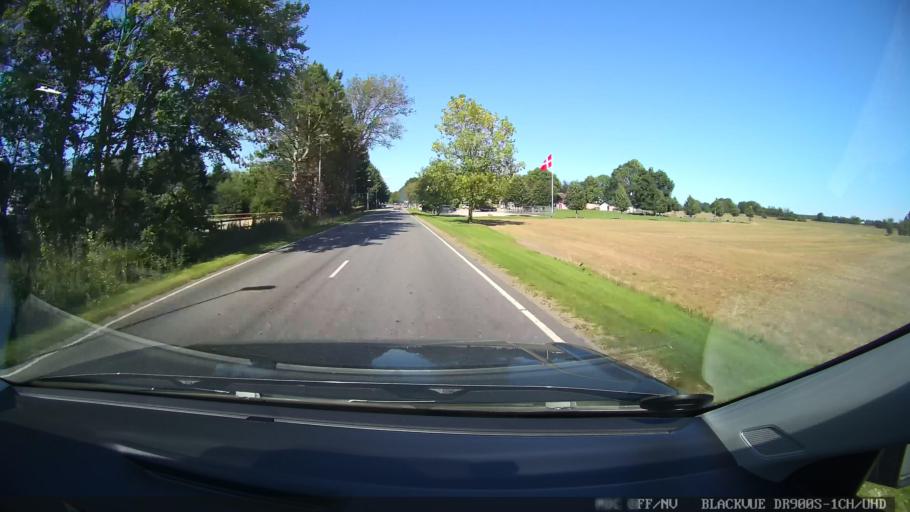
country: DK
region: Central Jutland
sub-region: Randers Kommune
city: Spentrup
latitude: 56.5526
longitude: 10.0020
